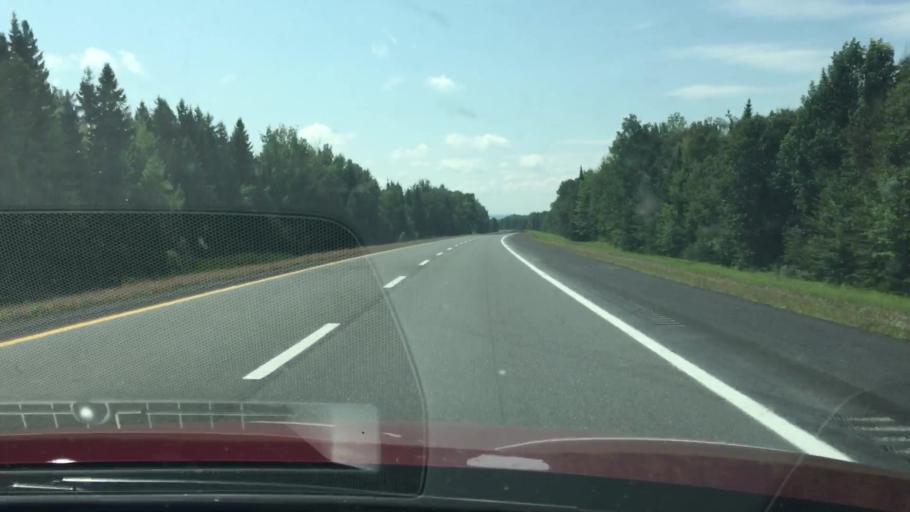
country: US
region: Maine
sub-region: Penobscot County
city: Patten
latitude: 45.9370
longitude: -68.3522
